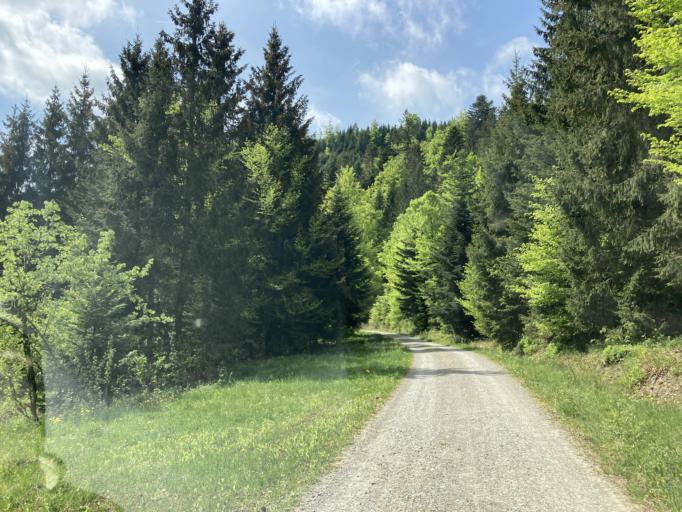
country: DE
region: Baden-Wuerttemberg
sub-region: Karlsruhe Region
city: Biberach
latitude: 48.5301
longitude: 8.2976
